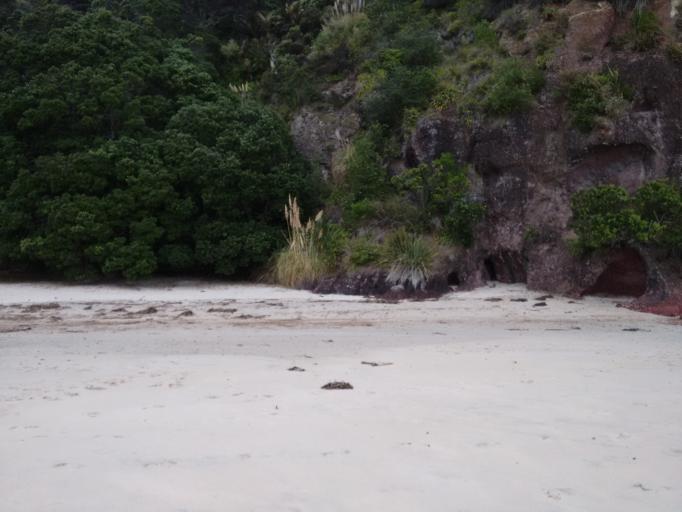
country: NZ
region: Waikato
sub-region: Thames-Coromandel District
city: Coromandel
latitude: -36.7005
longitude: 175.6095
